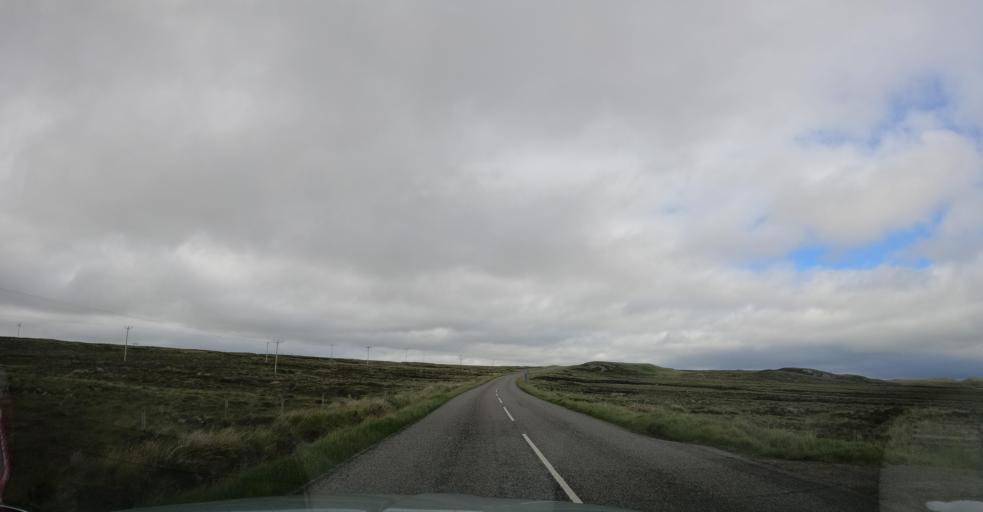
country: GB
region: Scotland
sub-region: Eilean Siar
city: Stornoway
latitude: 58.1608
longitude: -6.4941
